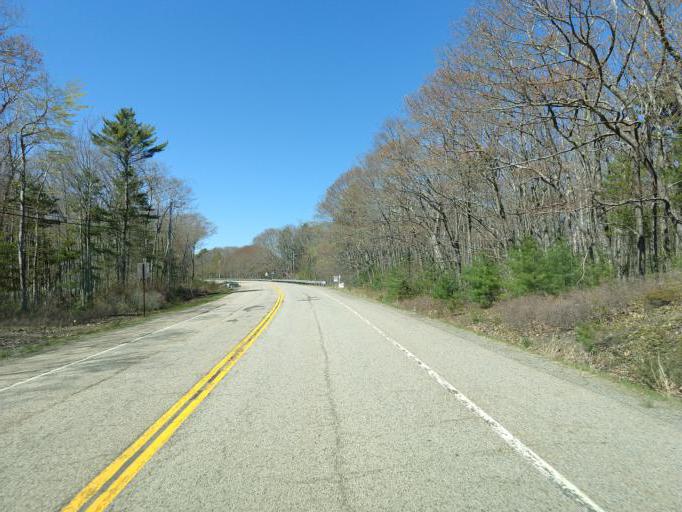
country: US
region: Maine
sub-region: York County
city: Old Orchard Beach
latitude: 43.4362
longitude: -70.3781
